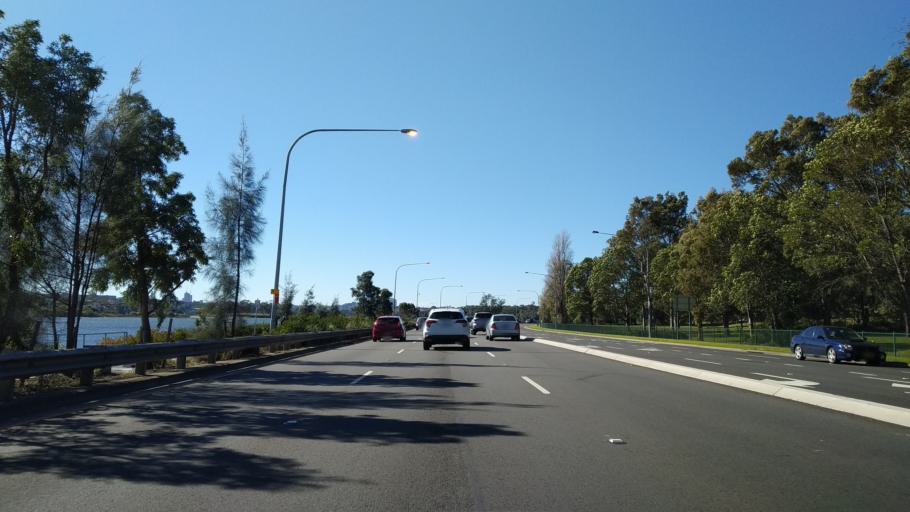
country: AU
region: New South Wales
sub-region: Canada Bay
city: Wareemba
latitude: -33.8707
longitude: 151.1421
